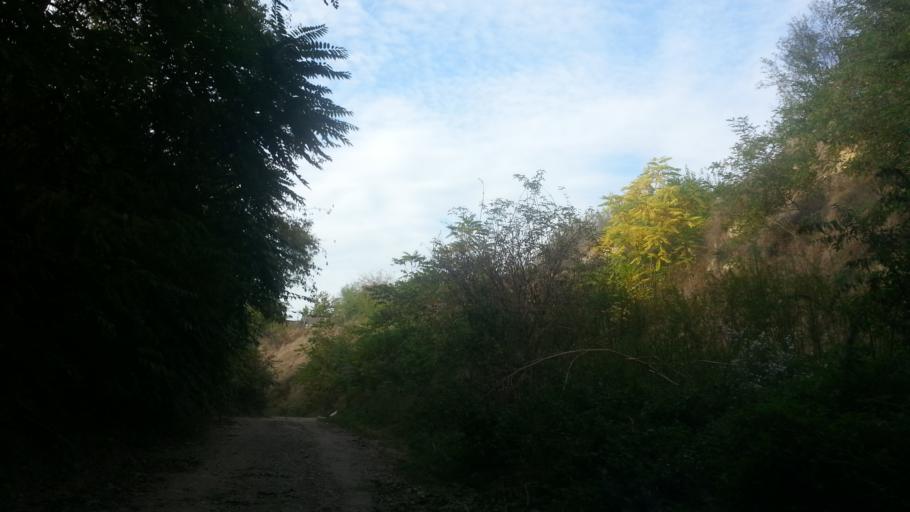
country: RS
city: Belegis
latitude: 45.0216
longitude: 20.3464
